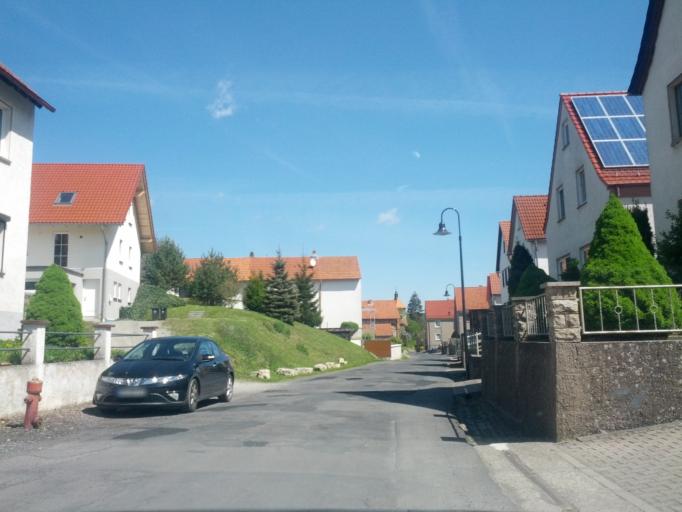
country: DE
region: Thuringia
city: Treffurt
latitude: 51.1026
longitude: 10.2172
